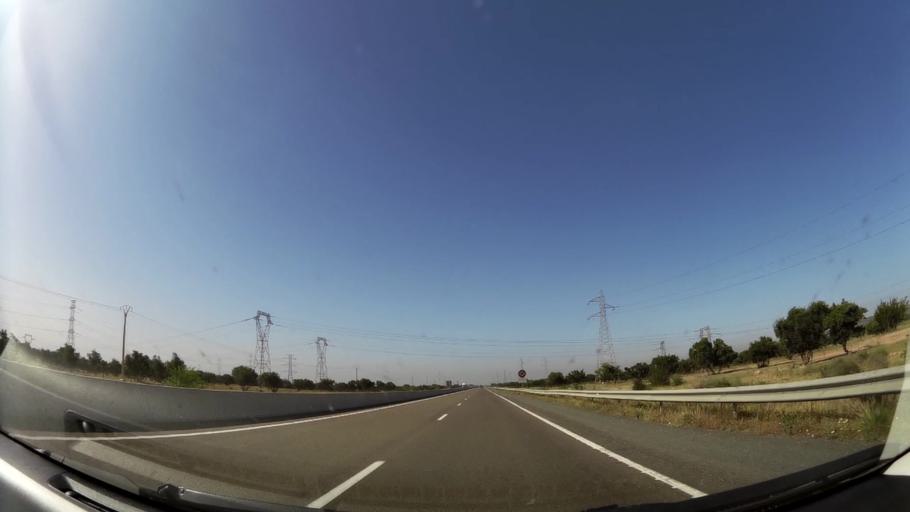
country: MA
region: Souss-Massa-Draa
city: Oulad Teima
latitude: 30.4452
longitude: -9.3666
